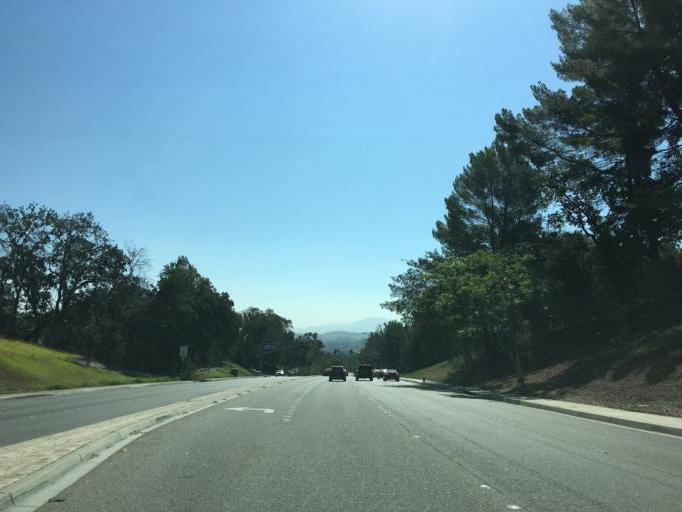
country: US
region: California
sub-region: Los Angeles County
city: Santa Clarita
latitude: 34.3947
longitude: -118.5668
